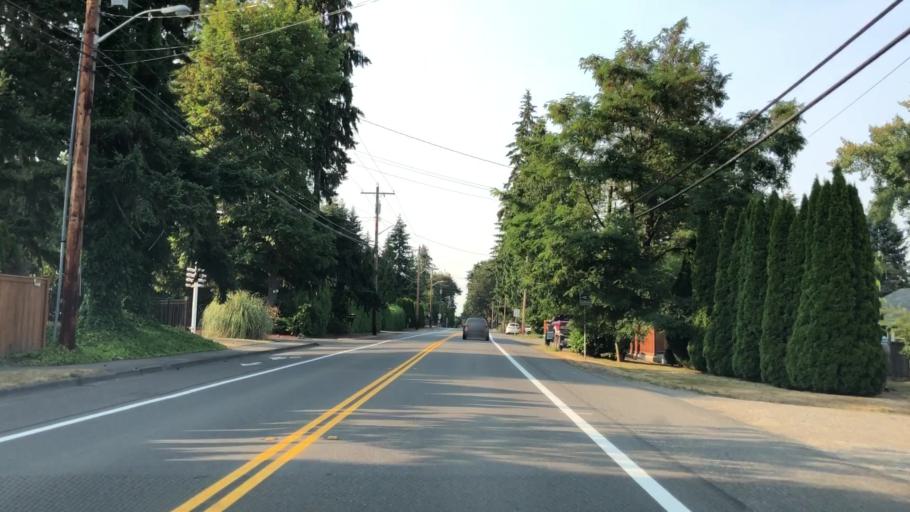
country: US
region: Washington
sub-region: King County
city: Kingsgate
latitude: 47.6936
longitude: -122.1648
